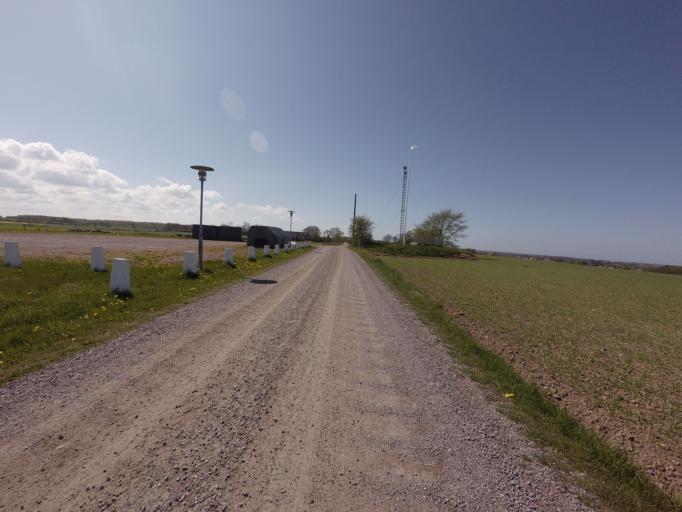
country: DK
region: Capital Region
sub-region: Helsingor Kommune
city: Helsingor
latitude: 56.1298
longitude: 12.6393
